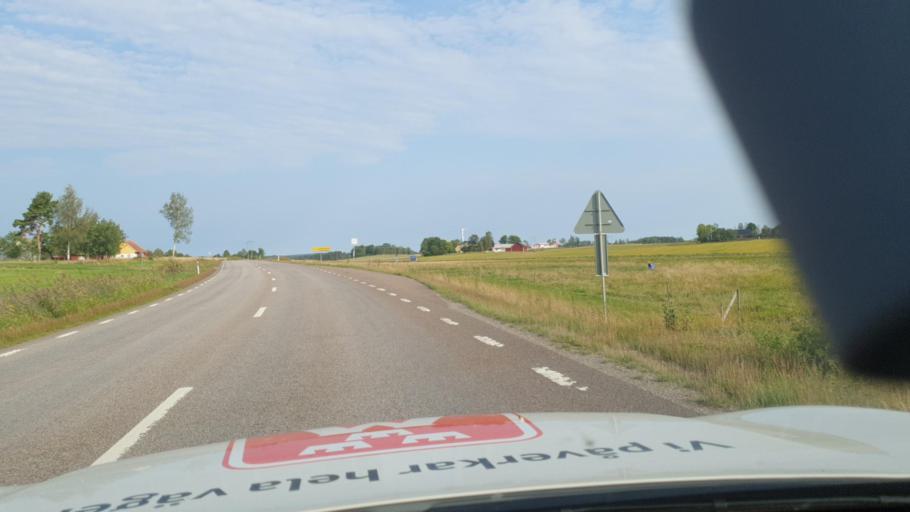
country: SE
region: Vaestra Goetaland
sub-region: Melleruds Kommun
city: Mellerud
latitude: 58.7214
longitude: 12.4557
